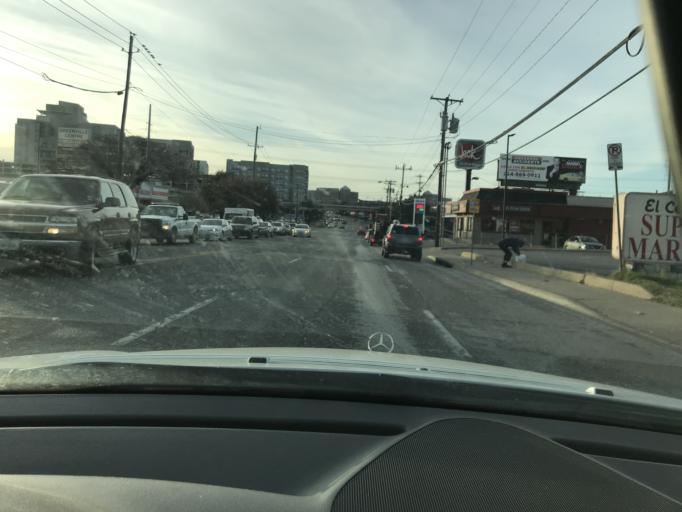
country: US
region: Texas
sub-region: Dallas County
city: University Park
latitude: 32.8715
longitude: -96.7630
